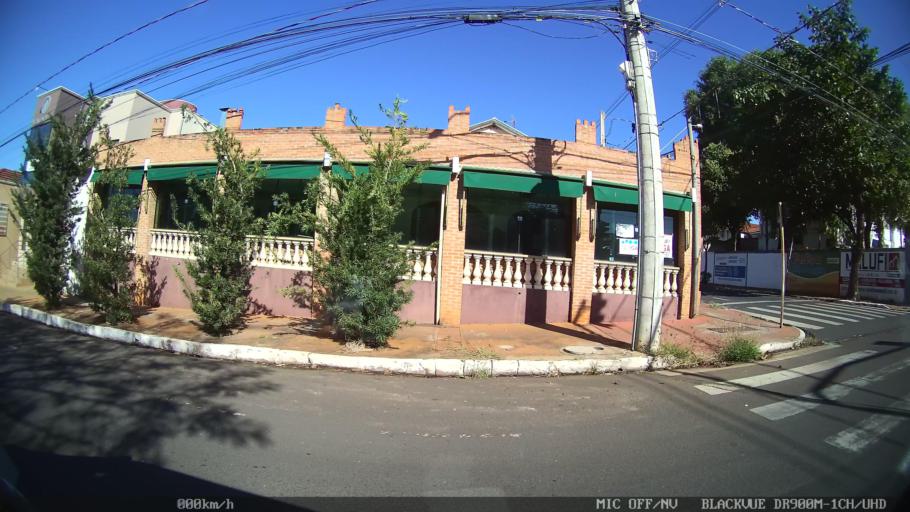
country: BR
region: Sao Paulo
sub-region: Olimpia
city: Olimpia
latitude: -20.7415
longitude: -48.9137
